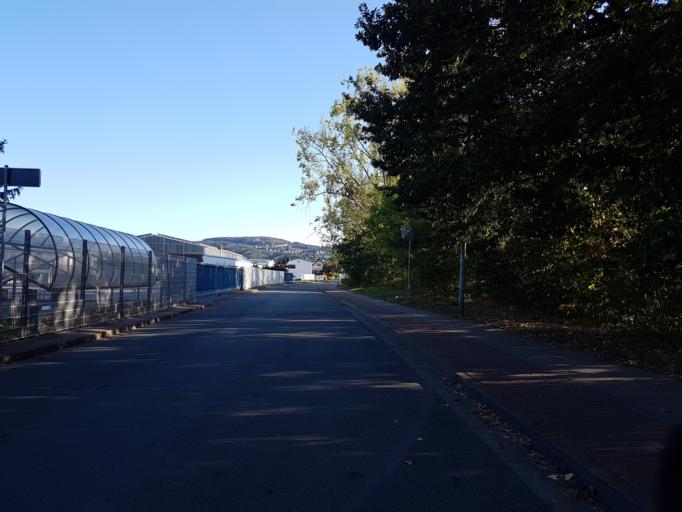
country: DE
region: North Rhine-Westphalia
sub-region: Regierungsbezirk Detmold
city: Vlotho
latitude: 52.1799
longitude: 8.8669
